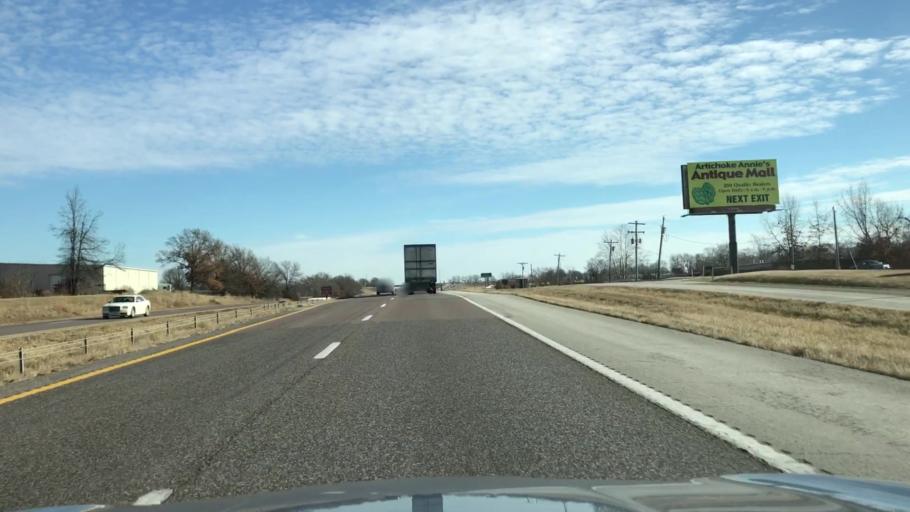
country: US
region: Missouri
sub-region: Boone County
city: Hallsville
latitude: 38.9538
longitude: -92.1392
